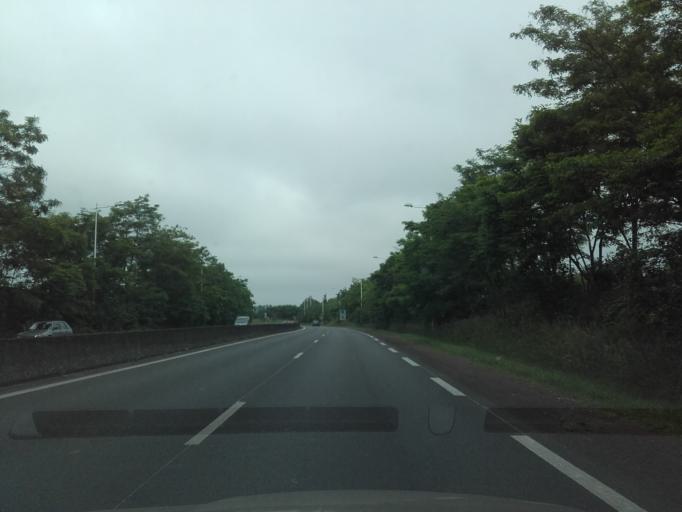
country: FR
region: Centre
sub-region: Departement d'Indre-et-Loire
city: Rochecorbon
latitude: 47.4174
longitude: 0.7182
